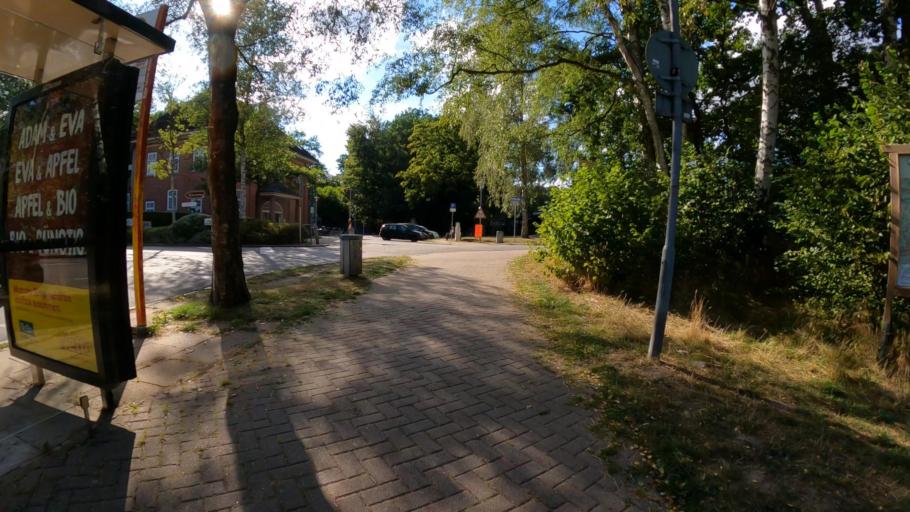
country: DE
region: Schleswig-Holstein
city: Ahrensburg
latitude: 53.6615
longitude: 10.2443
